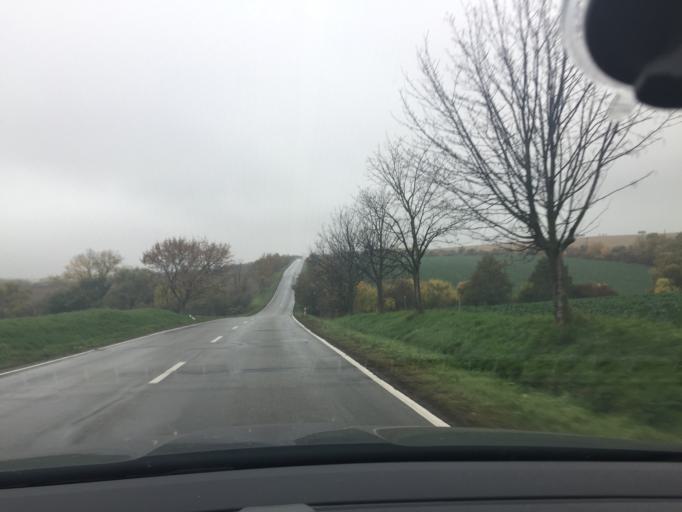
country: CZ
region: South Moravian
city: Rousinov
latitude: 49.1935
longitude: 16.8567
